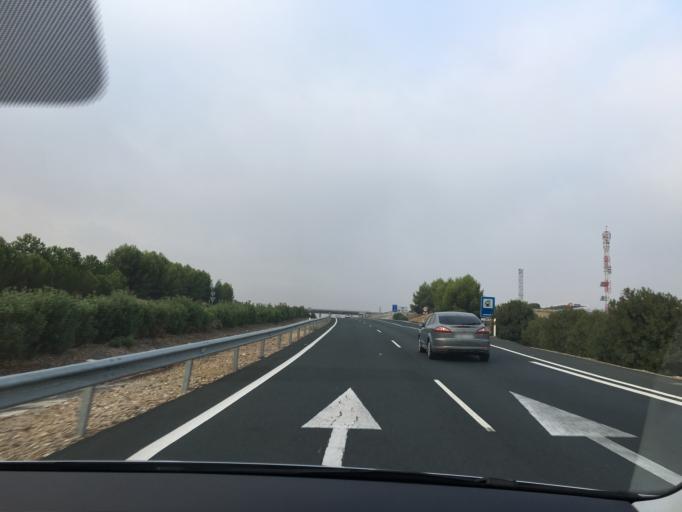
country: ES
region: Andalusia
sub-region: Province of Cordoba
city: La Carlota
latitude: 37.7000
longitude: -4.9172
